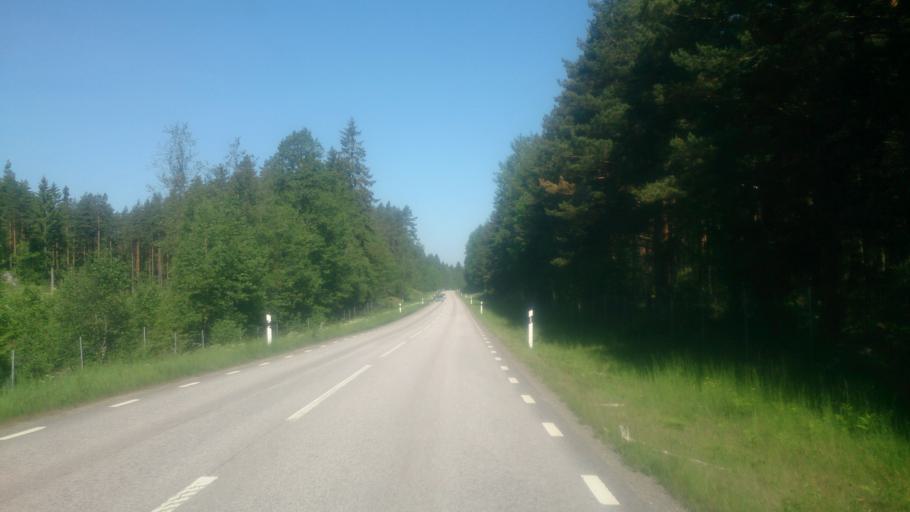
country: SE
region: OEstergoetland
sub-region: Atvidabergs Kommun
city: Atvidaberg
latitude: 58.1672
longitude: 16.0492
